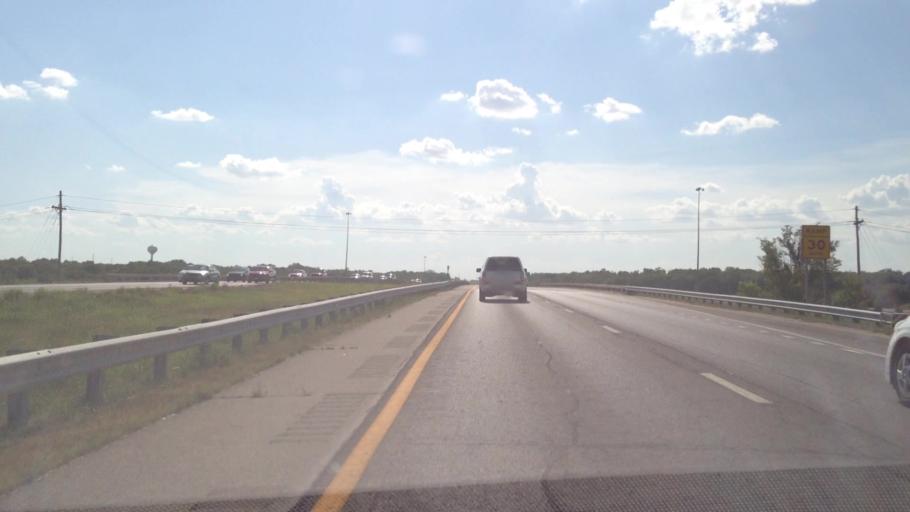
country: US
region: Kansas
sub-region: Johnson County
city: De Soto
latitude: 38.9612
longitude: -94.9813
